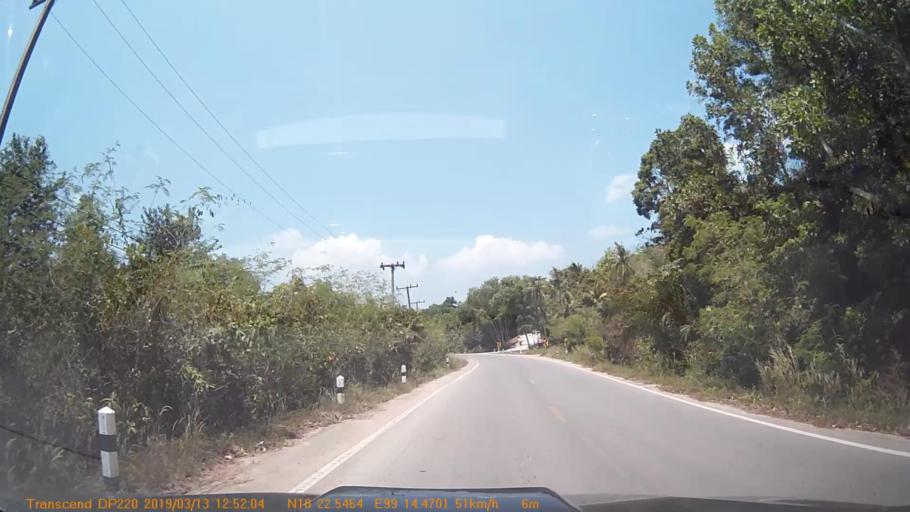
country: TH
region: Chumphon
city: Chumphon
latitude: 10.3760
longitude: 99.2410
